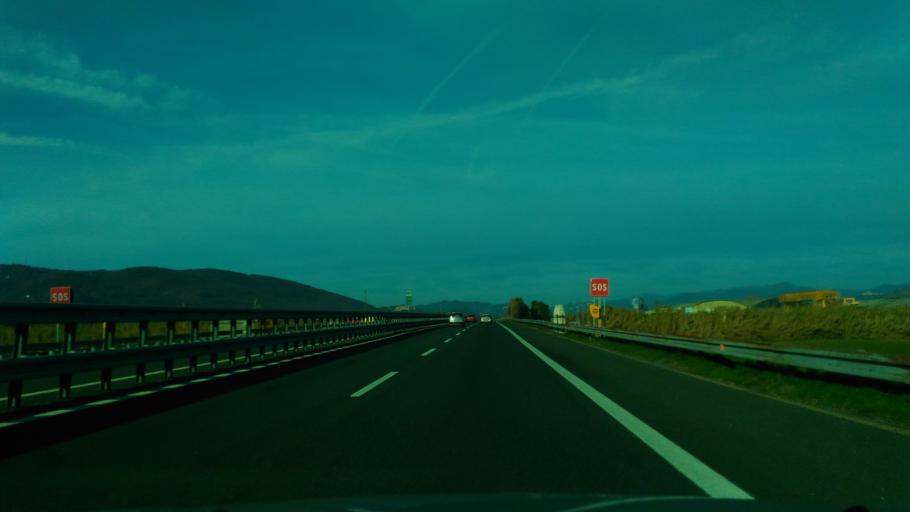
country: IT
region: Liguria
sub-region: Provincia di La Spezia
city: Colombiera-Molicciara
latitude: 44.0657
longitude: 10.0001
